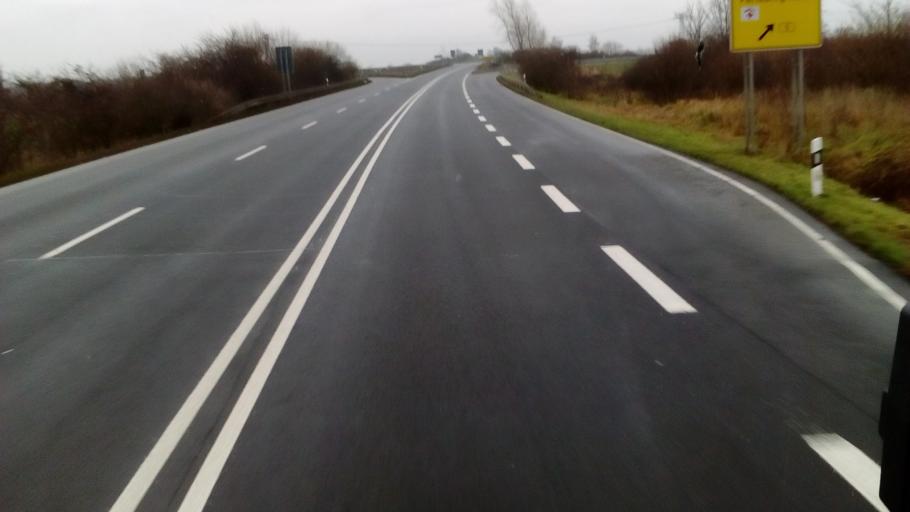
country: DE
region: Brandenburg
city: Perleberg
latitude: 53.0881
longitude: 11.8396
